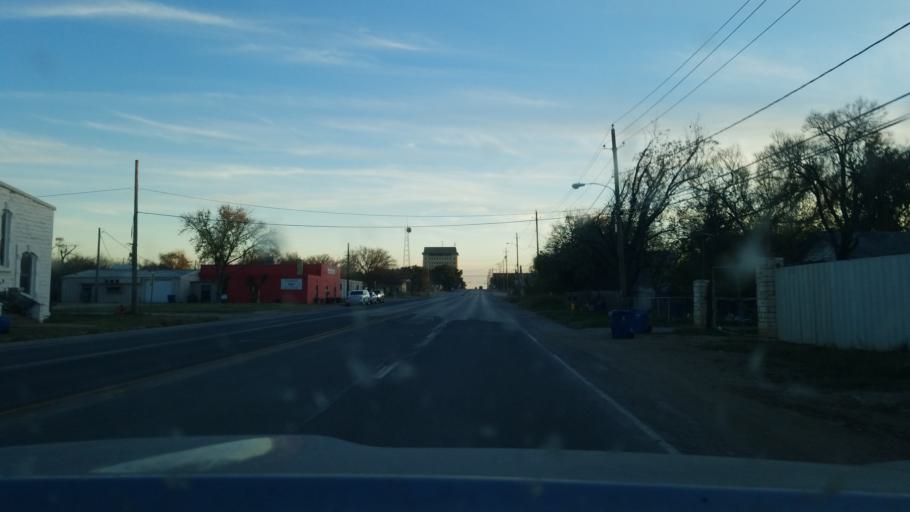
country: US
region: Texas
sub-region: Stephens County
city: Breckenridge
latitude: 32.7610
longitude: -98.9027
